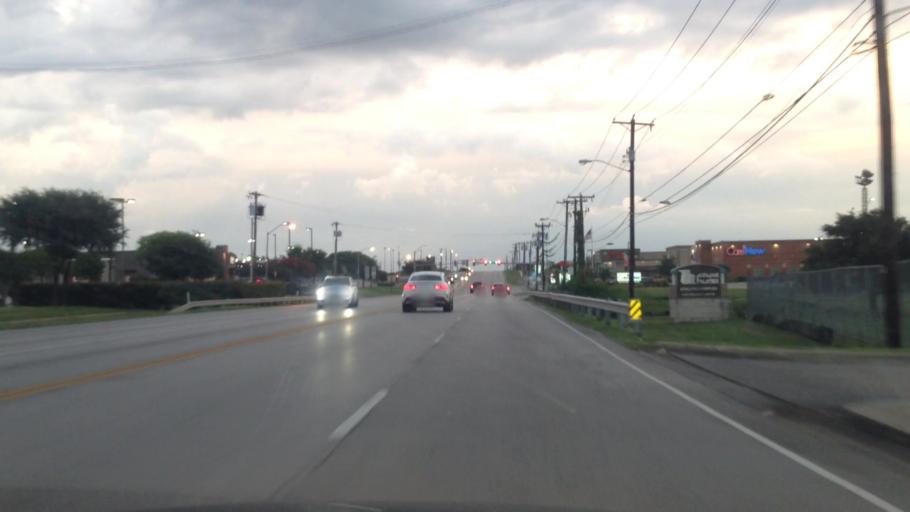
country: US
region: Texas
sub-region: Tarrant County
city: Hurst
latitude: 32.8560
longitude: -97.1858
